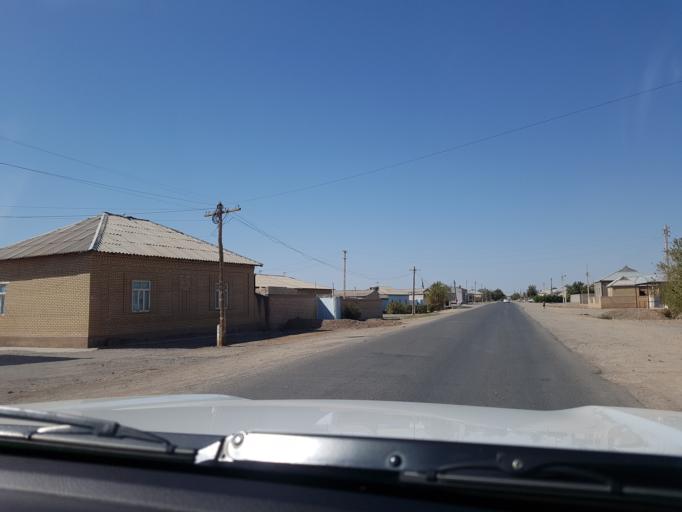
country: IR
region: Razavi Khorasan
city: Sarakhs
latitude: 36.5159
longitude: 61.2212
